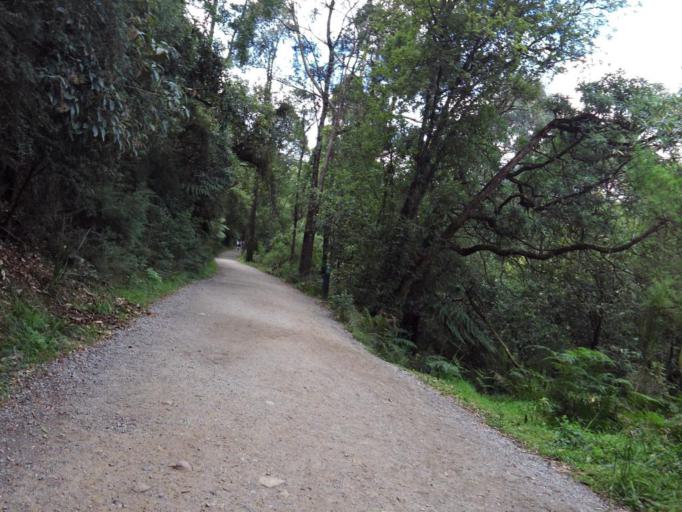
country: AU
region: Victoria
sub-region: Yarra Ranges
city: Ferny Creek
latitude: -37.8777
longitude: 145.3178
